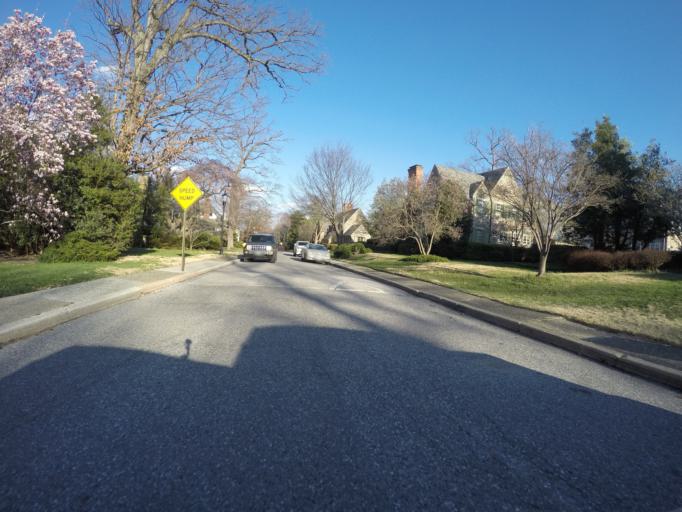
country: US
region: Maryland
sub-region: Baltimore County
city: Towson
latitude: 39.3545
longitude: -76.6193
